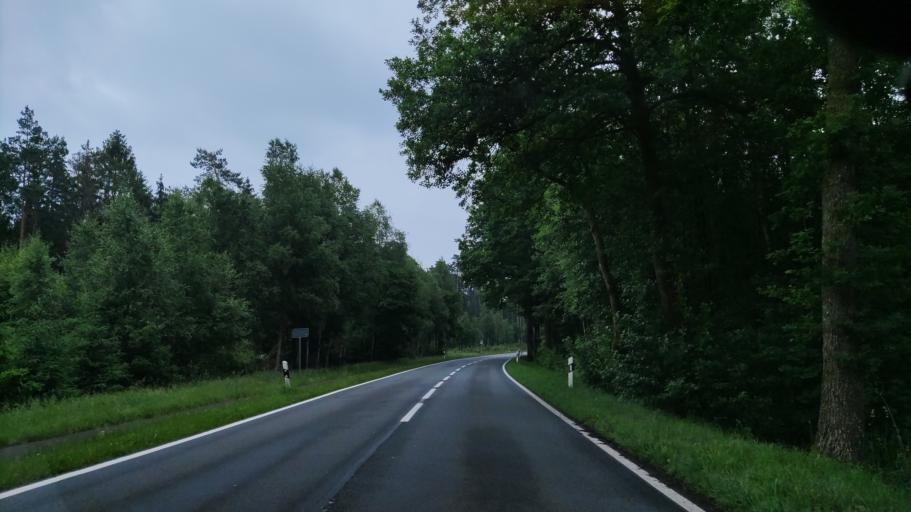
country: DE
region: Lower Saxony
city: Fassberg
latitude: 52.8894
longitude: 10.1654
